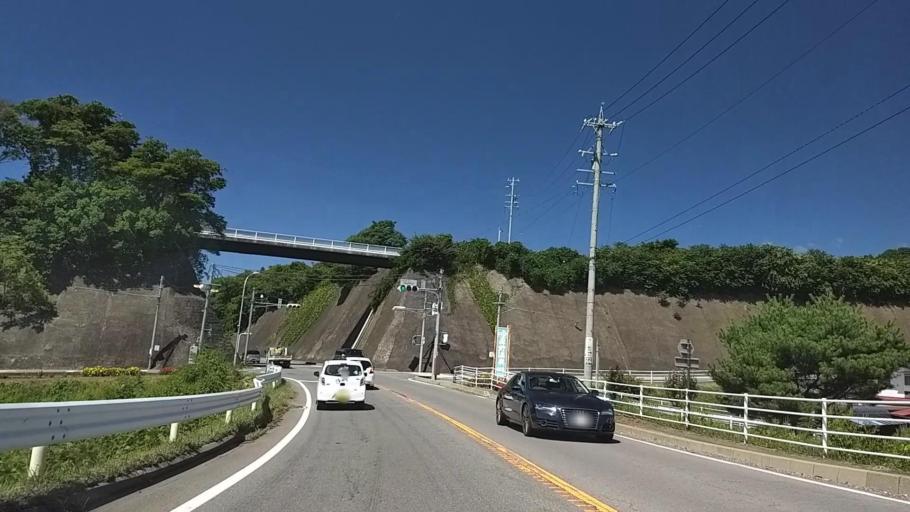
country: JP
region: Nagano
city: Komoro
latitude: 36.3490
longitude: 138.4316
